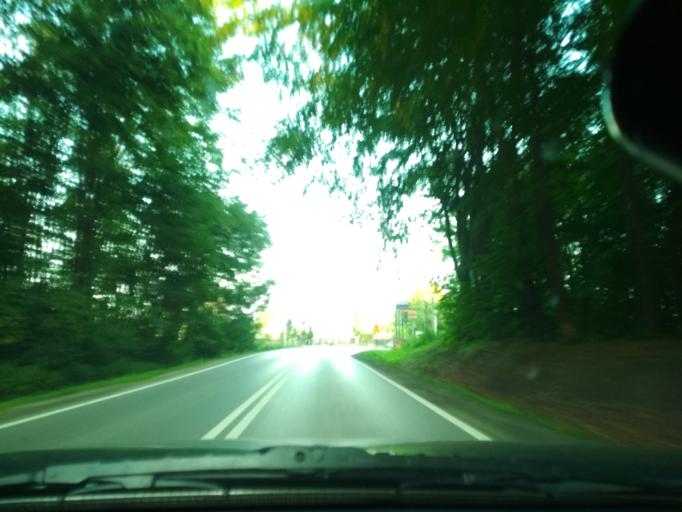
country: PL
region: Lesser Poland Voivodeship
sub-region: Powiat olkuski
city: Wolbrom
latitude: 50.3944
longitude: 19.7417
